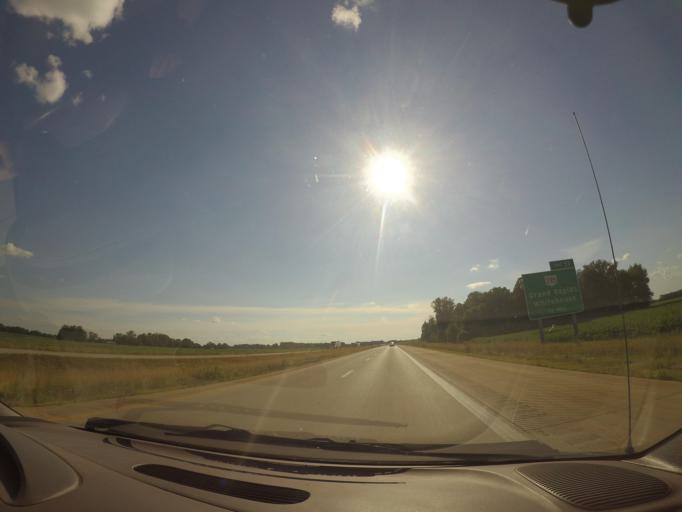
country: US
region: Ohio
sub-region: Lucas County
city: Whitehouse
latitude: 41.4561
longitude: -83.8083
